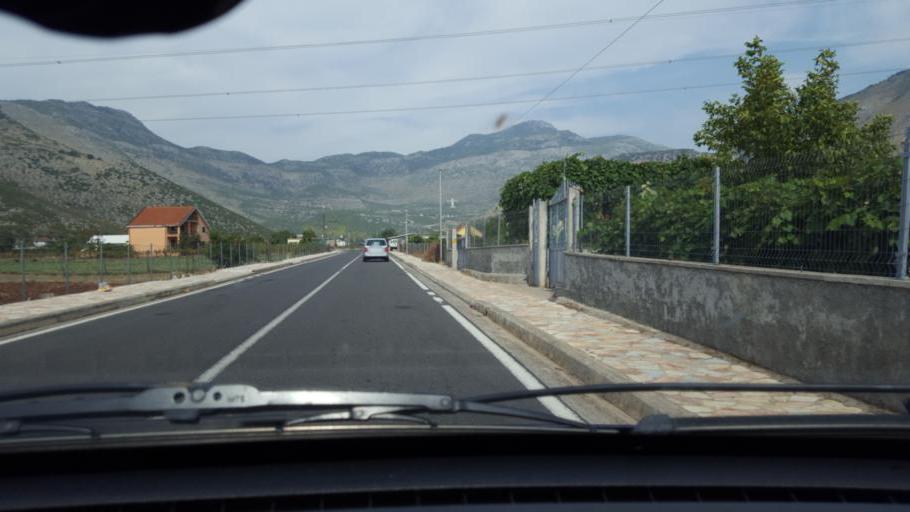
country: AL
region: Shkoder
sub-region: Rrethi i Malesia e Madhe
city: Hot
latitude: 42.3436
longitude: 19.4392
